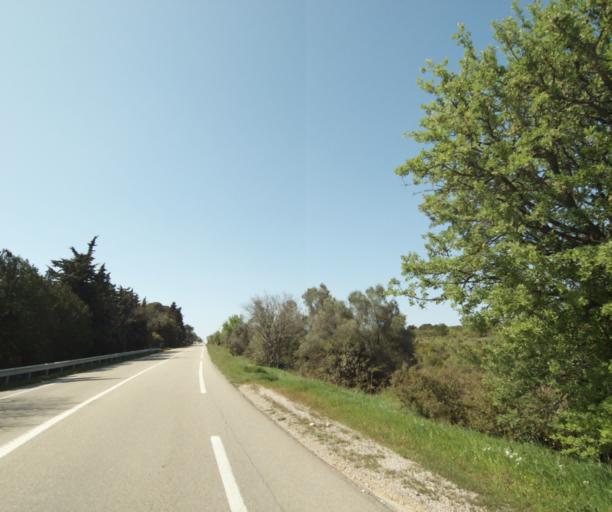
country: FR
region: Languedoc-Roussillon
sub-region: Departement de l'Herault
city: Murviel-les-Montpellier
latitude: 43.6362
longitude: 3.7544
